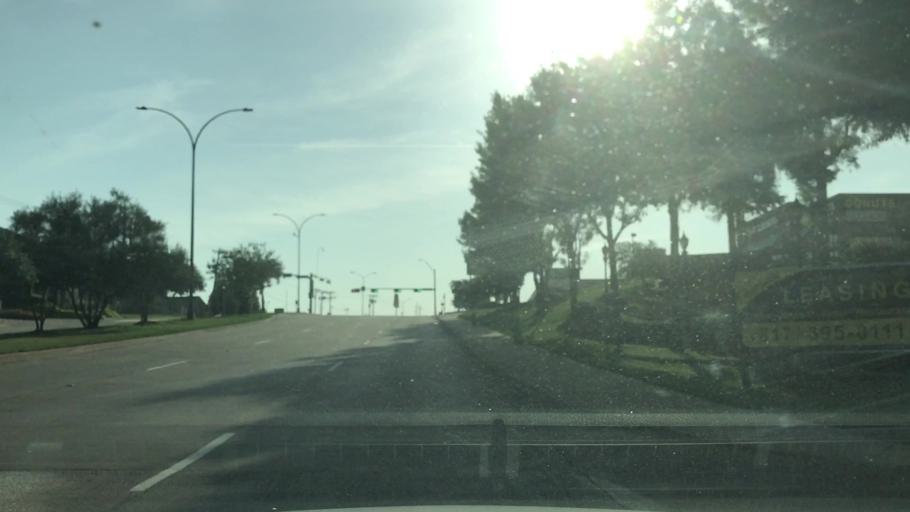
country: US
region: Texas
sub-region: Tarrant County
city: Euless
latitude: 32.7849
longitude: -97.0640
